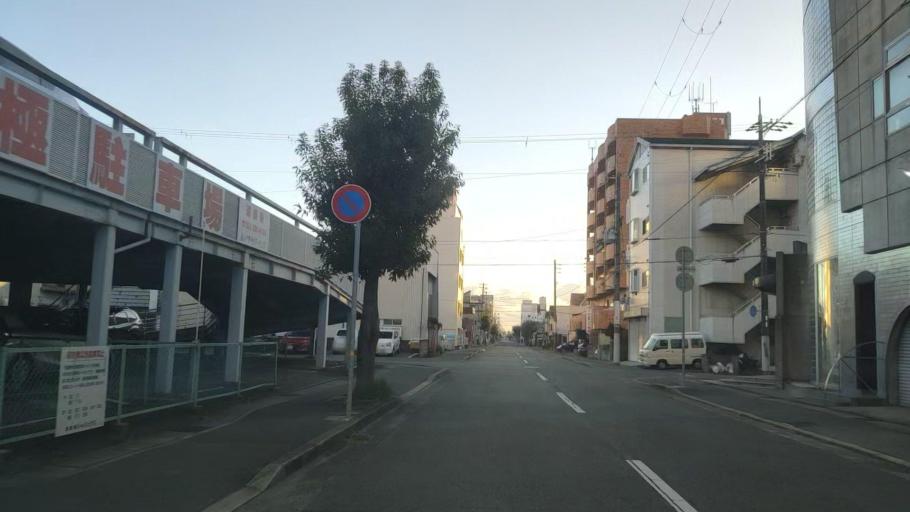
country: JP
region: Hyogo
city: Himeji
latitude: 34.8255
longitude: 134.6854
